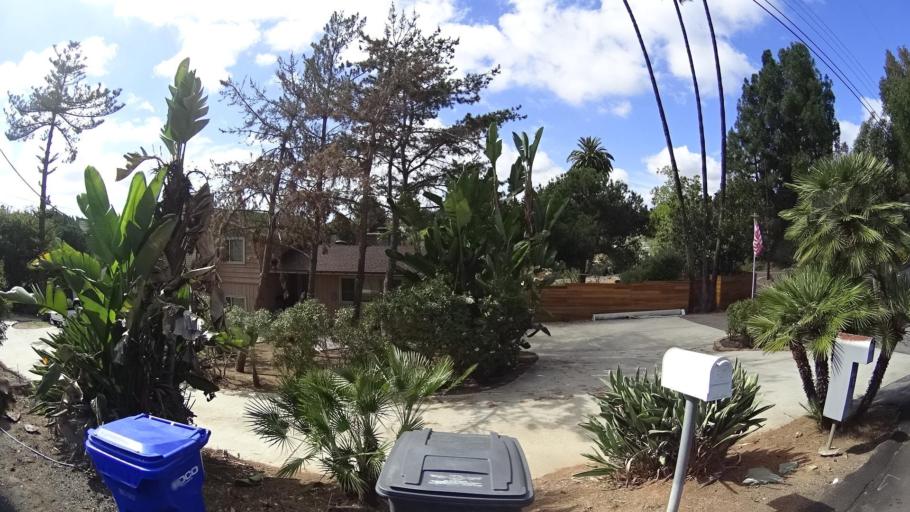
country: US
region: California
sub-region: San Diego County
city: Casa de Oro-Mount Helix
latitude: 32.7600
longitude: -116.9597
